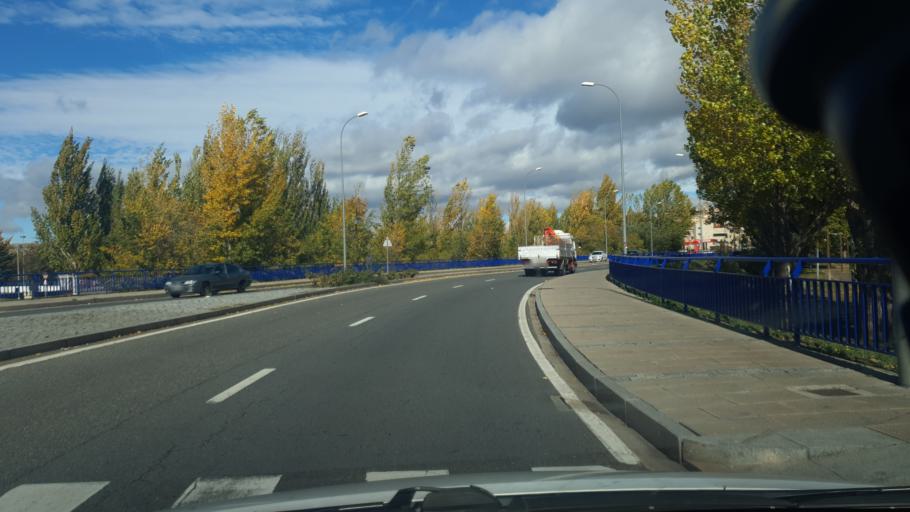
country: ES
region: Castille and Leon
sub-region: Provincia de Avila
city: Avila
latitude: 40.6462
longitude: -4.7044
